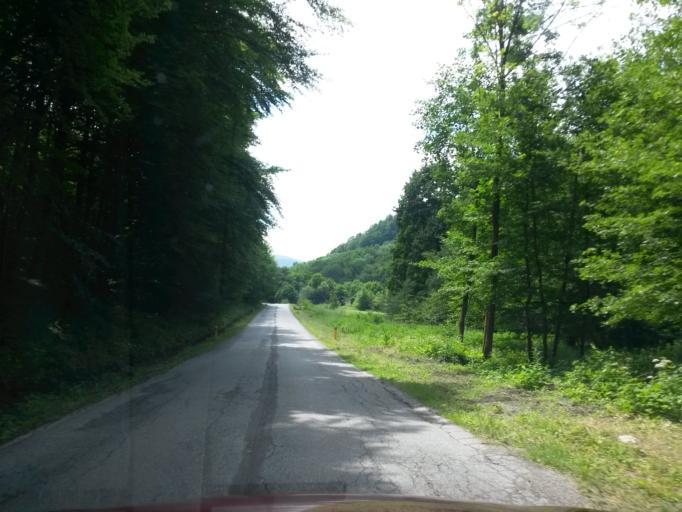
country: SK
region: Kosicky
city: Gelnica
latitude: 48.9150
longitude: 21.0314
